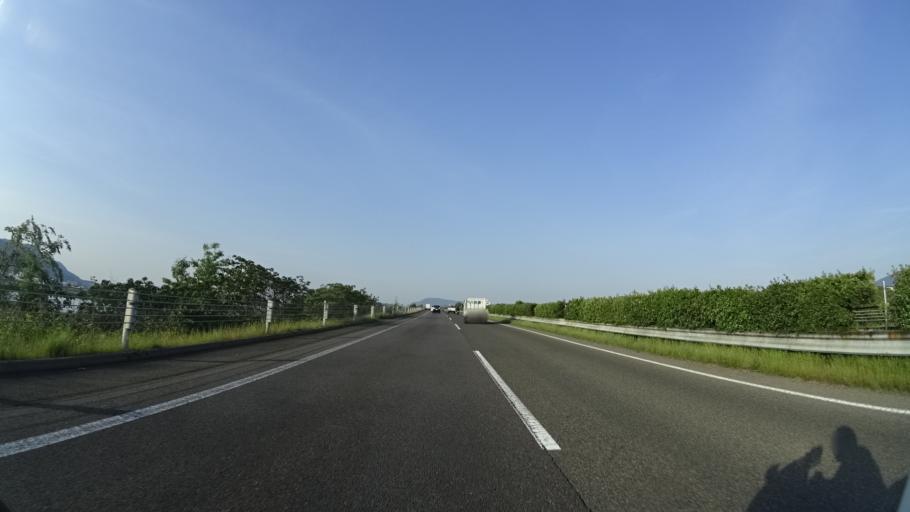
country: JP
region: Kagawa
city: Kan'onjicho
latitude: 34.1105
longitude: 133.6816
